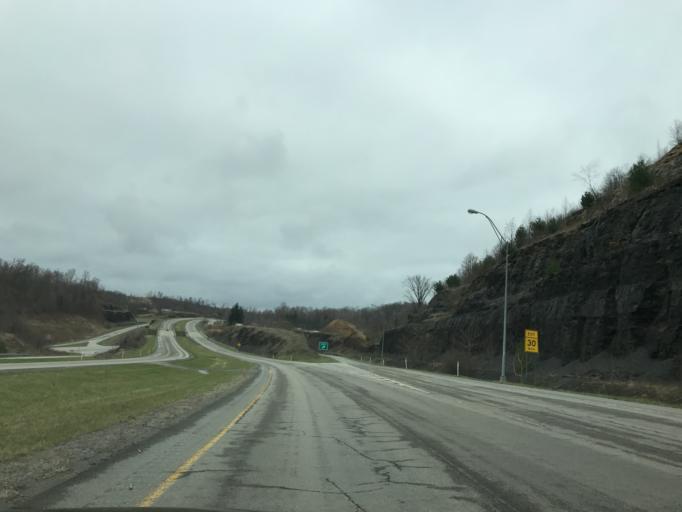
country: US
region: West Virginia
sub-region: Raleigh County
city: Sophia
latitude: 37.7152
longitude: -81.2563
